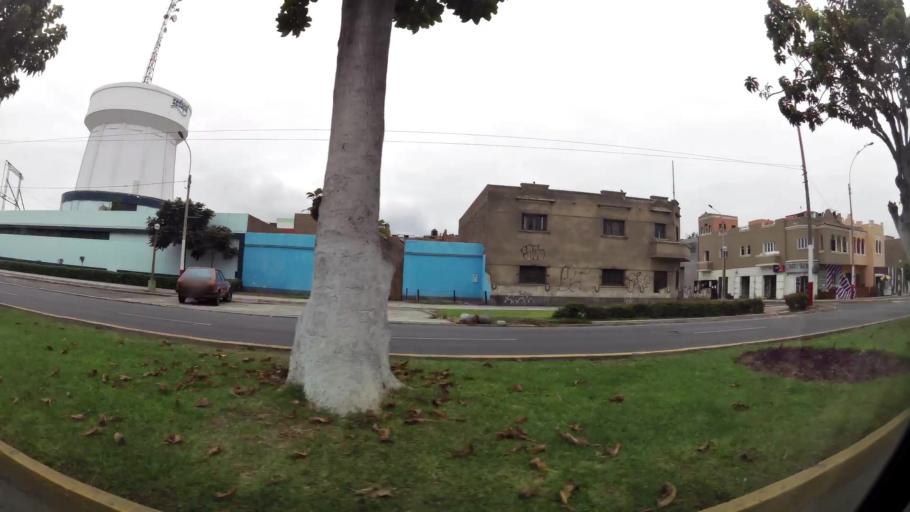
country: PE
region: Callao
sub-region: Callao
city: Callao
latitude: -12.0568
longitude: -77.1317
